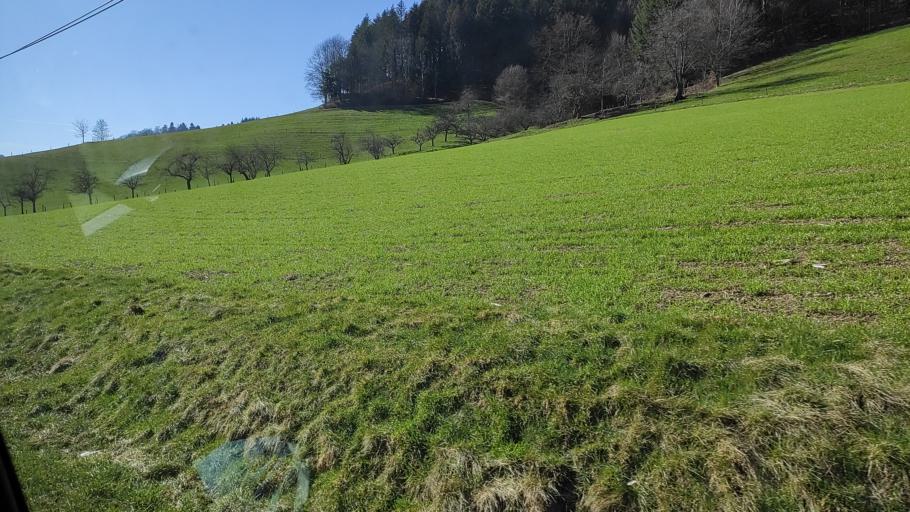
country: DE
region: Baden-Wuerttemberg
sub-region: Freiburg Region
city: Gutach im Breisgau
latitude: 48.1496
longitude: 7.9780
